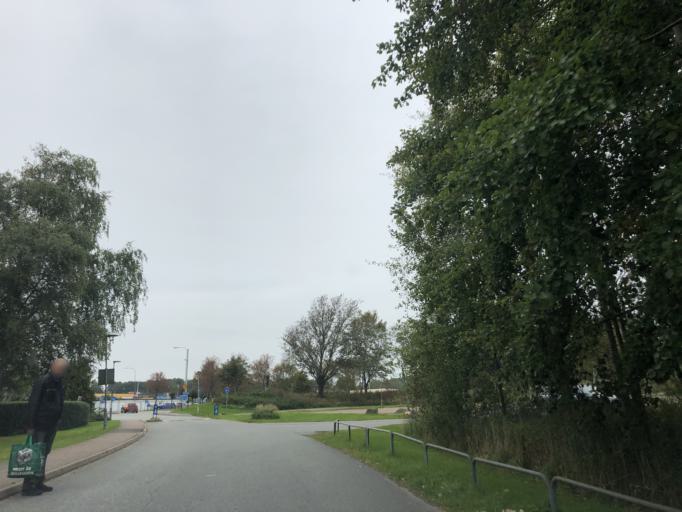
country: SE
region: Vaestra Goetaland
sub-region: Goteborg
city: Majorna
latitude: 57.6557
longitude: 11.8809
